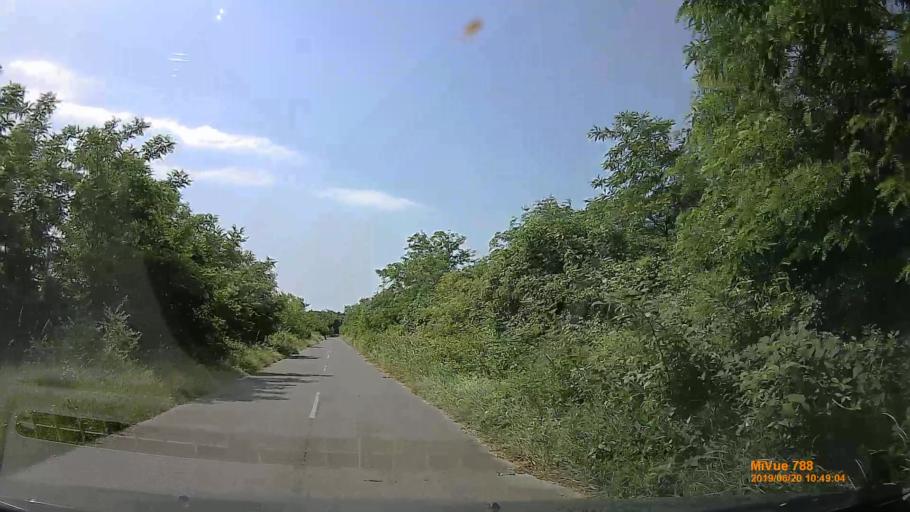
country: HU
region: Baranya
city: Mecseknadasd
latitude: 46.1632
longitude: 18.5831
